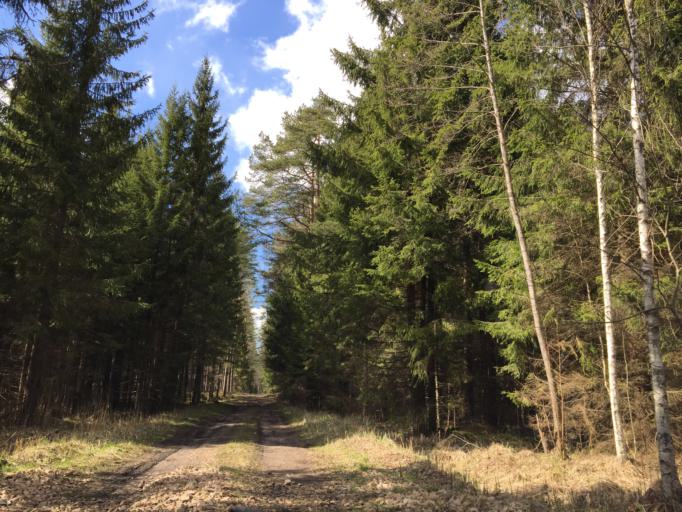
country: LV
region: Garkalne
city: Garkalne
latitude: 56.9514
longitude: 24.4725
